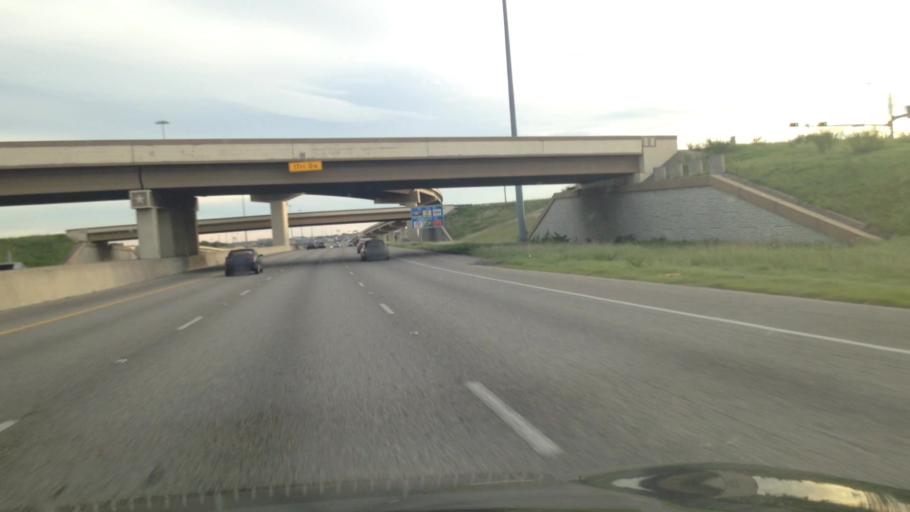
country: US
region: Texas
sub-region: Travis County
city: Onion Creek
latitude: 30.1131
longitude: -97.8069
